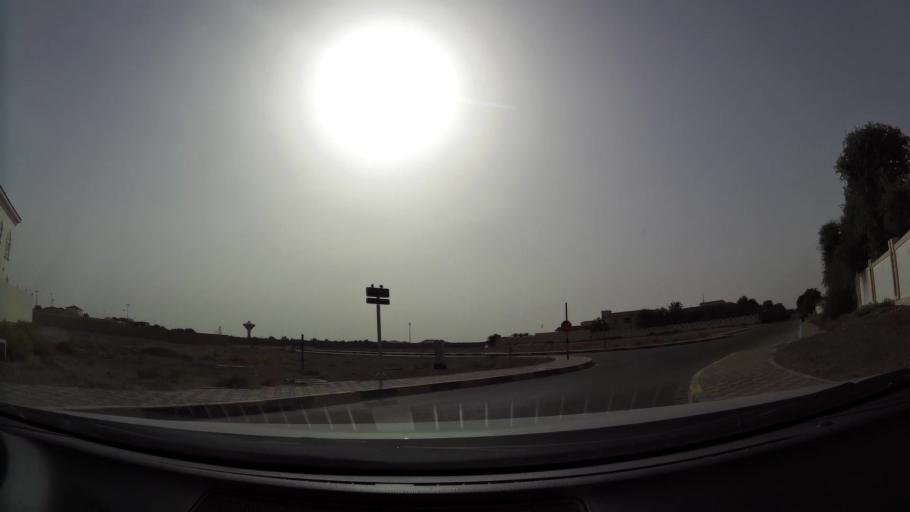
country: AE
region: Abu Dhabi
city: Al Ain
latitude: 24.1887
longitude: 55.6038
